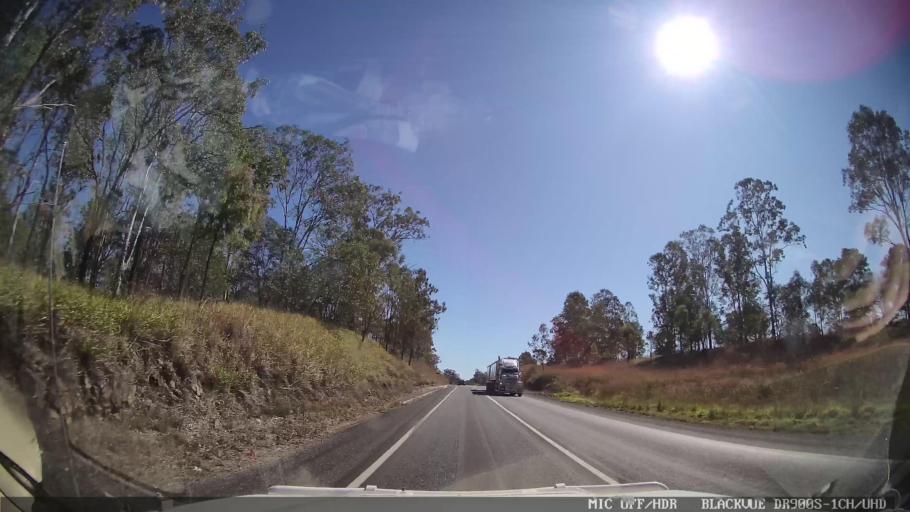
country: AU
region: Queensland
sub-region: Gympie Regional Council
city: Gympie
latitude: -26.0384
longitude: 152.5697
